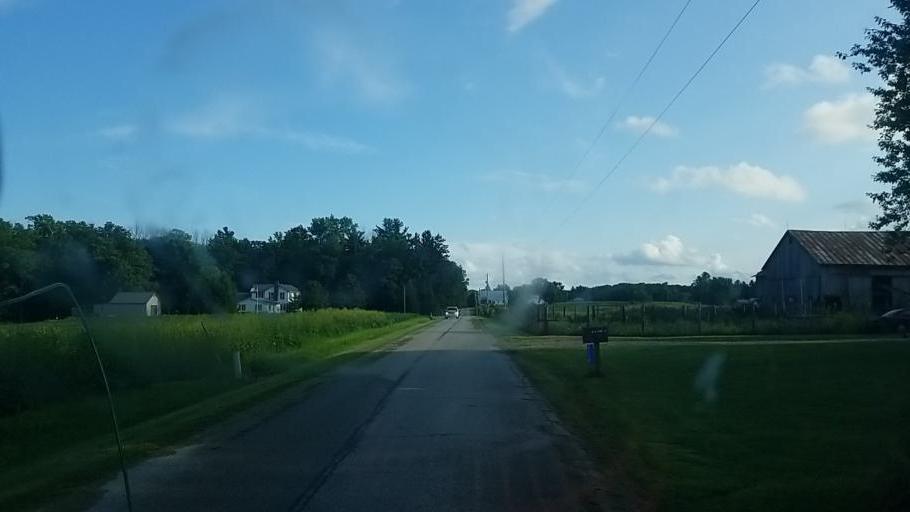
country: US
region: Ohio
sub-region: Crawford County
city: Bucyrus
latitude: 40.7800
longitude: -83.0553
